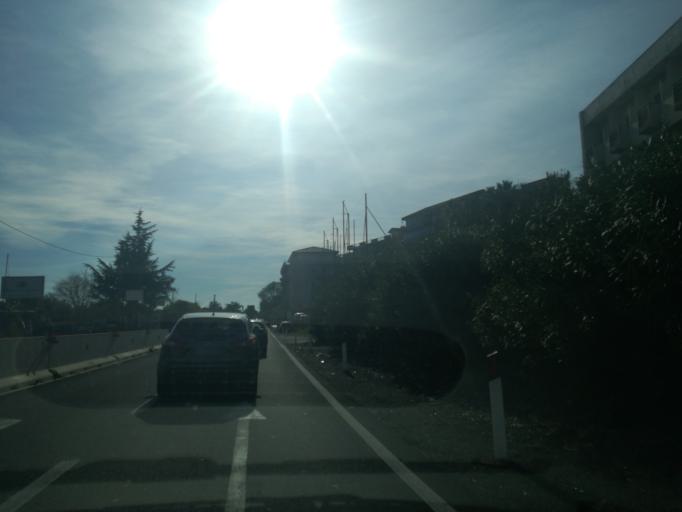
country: IT
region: Sicily
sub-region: Catania
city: Acireale
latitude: 37.6038
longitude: 15.1691
